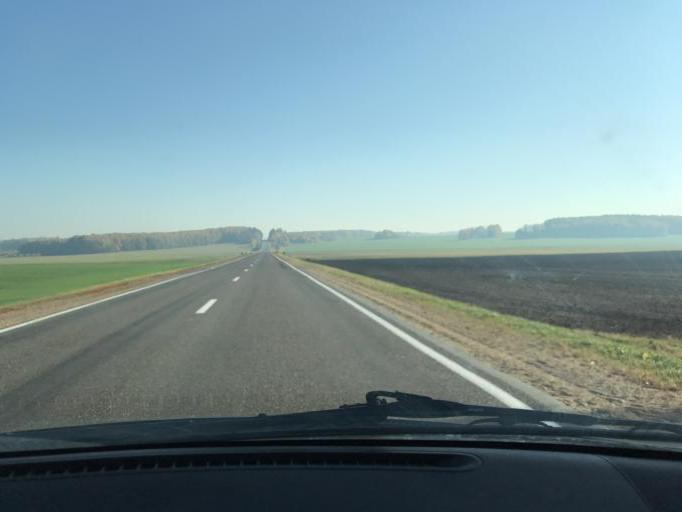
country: BY
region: Minsk
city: Klyetsk
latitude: 52.9682
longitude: 26.5966
